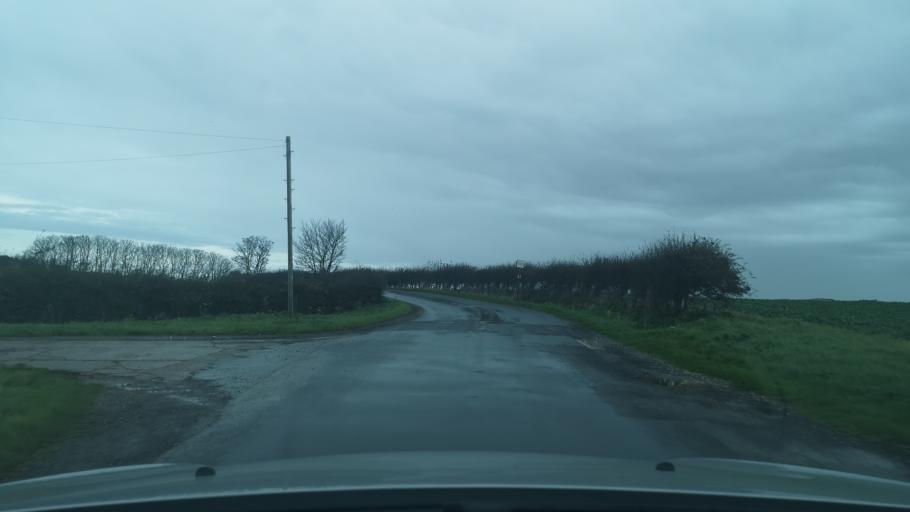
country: GB
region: England
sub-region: East Riding of Yorkshire
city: Holmpton
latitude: 53.6729
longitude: 0.0913
